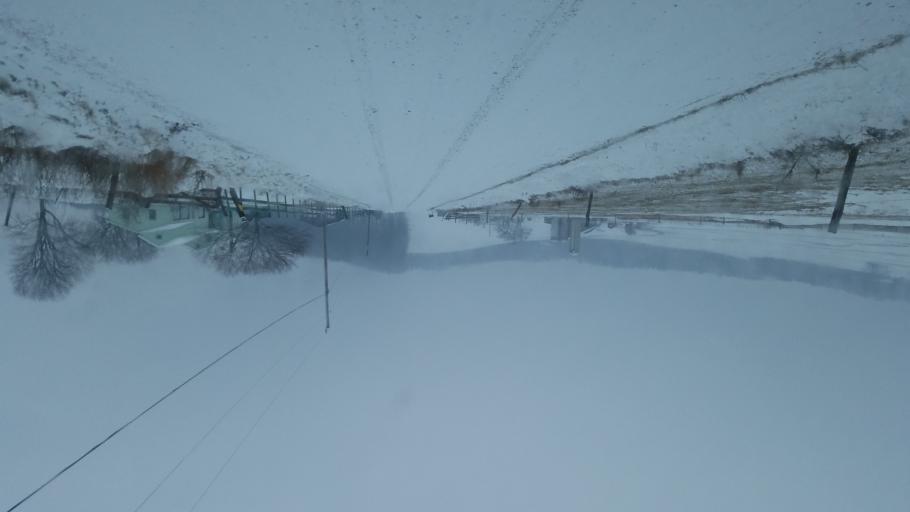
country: US
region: New York
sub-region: Steuben County
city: Canisteo
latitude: 42.1294
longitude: -77.5265
